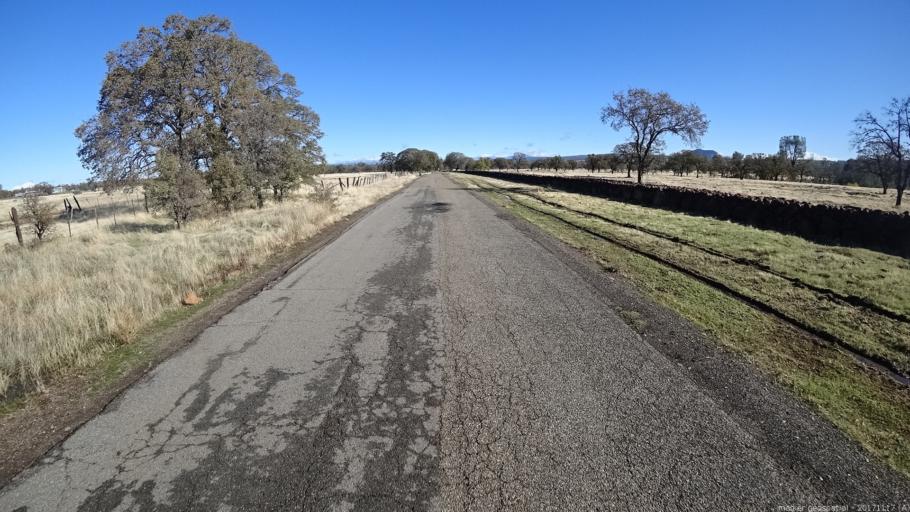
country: US
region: California
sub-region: Shasta County
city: Palo Cedro
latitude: 40.4543
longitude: -122.1078
